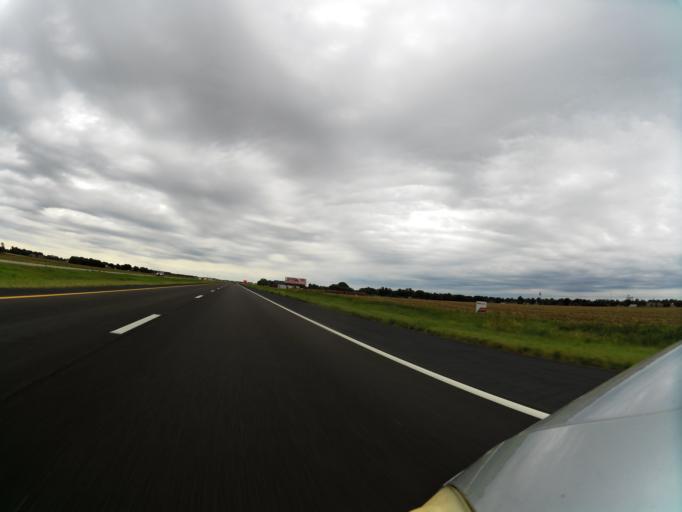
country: US
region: Kansas
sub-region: Reno County
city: Haven
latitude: 37.8761
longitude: -97.6738
